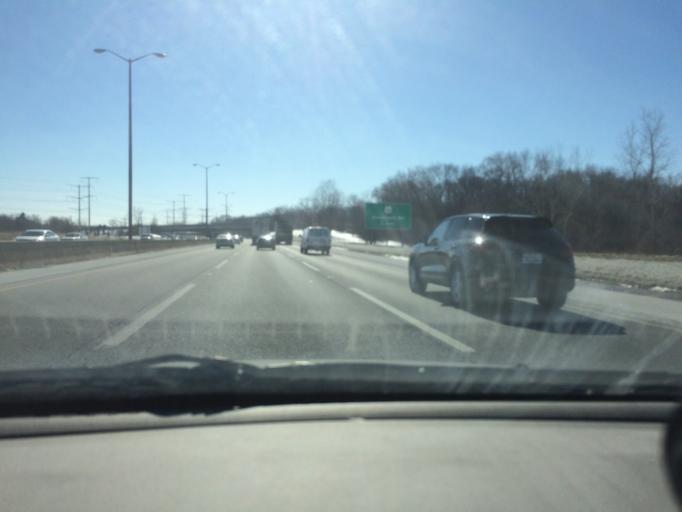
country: US
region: Illinois
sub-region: DuPage County
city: Lombard
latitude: 41.8924
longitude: -88.0378
